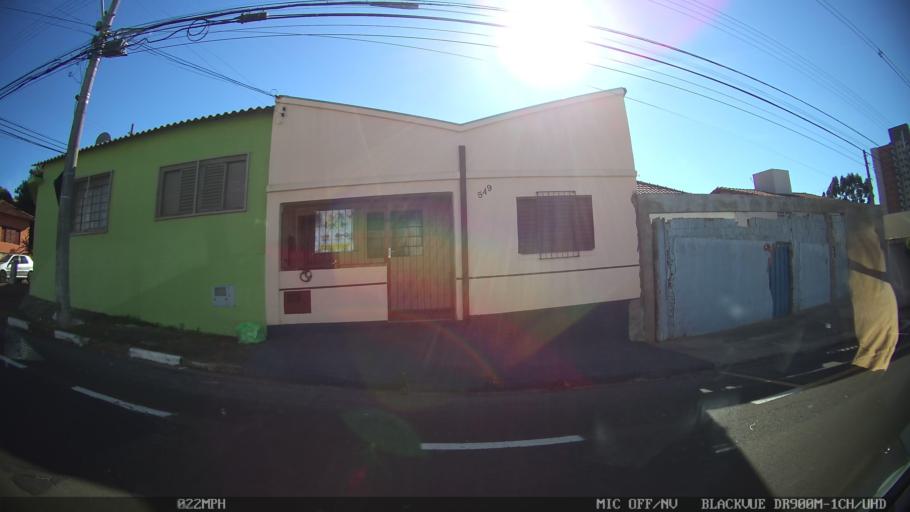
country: BR
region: Sao Paulo
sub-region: Franca
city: Franca
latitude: -20.5298
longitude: -47.4074
